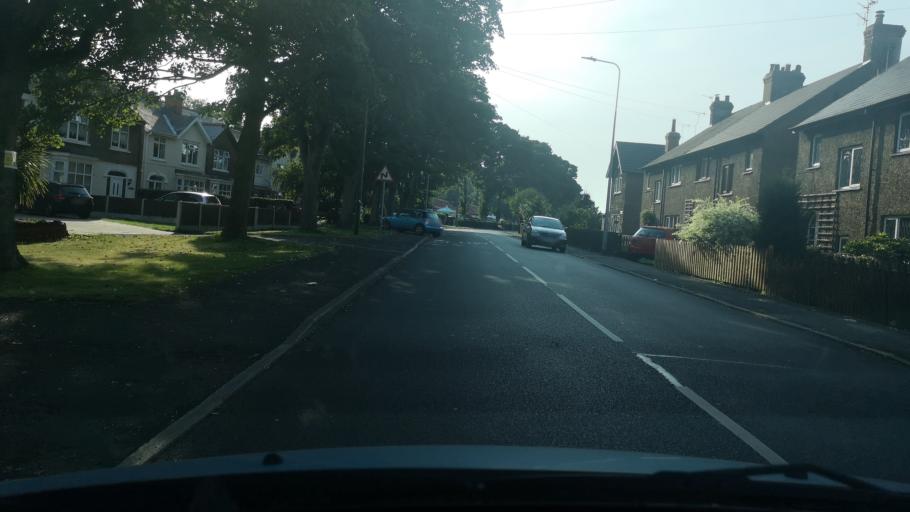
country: GB
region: England
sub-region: North Lincolnshire
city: Scunthorpe
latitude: 53.5846
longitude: -0.6562
